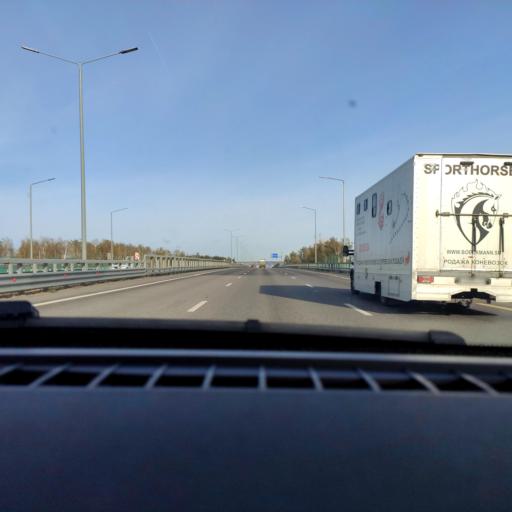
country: RU
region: Voronezj
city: Somovo
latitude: 51.7344
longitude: 39.3101
